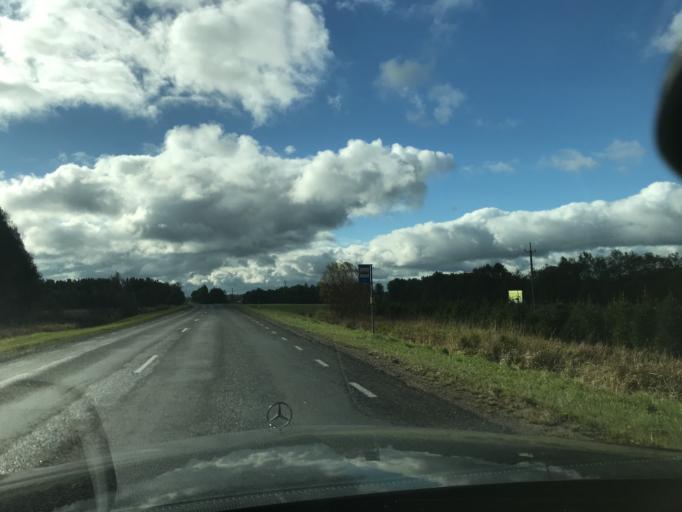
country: EE
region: Tartu
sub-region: Elva linn
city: Elva
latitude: 57.9901
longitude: 26.2629
